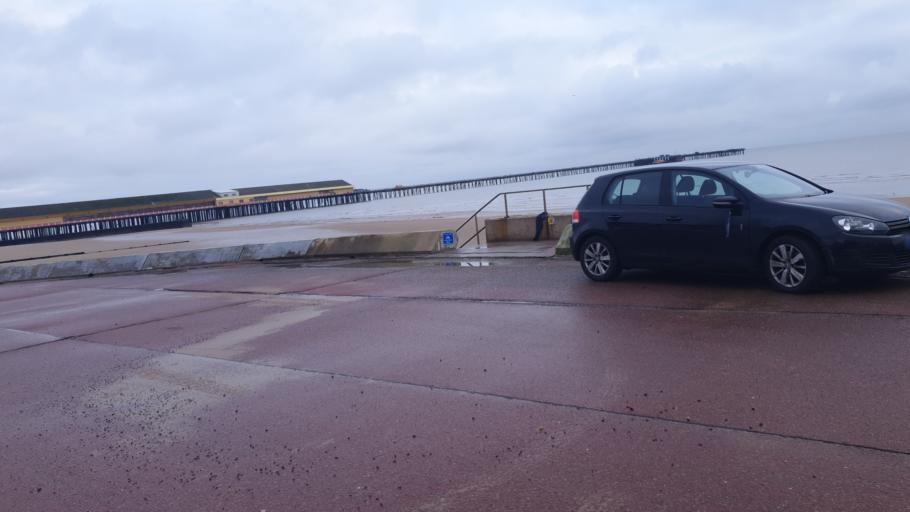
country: GB
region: England
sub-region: Essex
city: Walton-on-the-Naze
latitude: 51.8443
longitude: 1.2682
